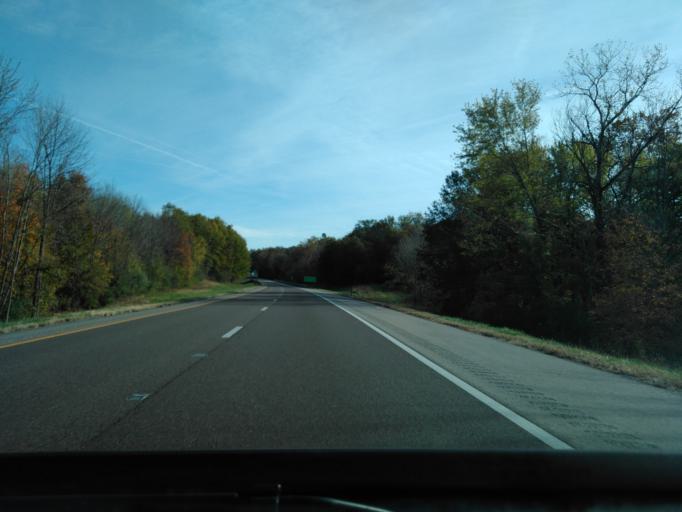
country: US
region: Illinois
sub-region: Madison County
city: Saint Jacob
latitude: 38.7667
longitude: -89.7582
